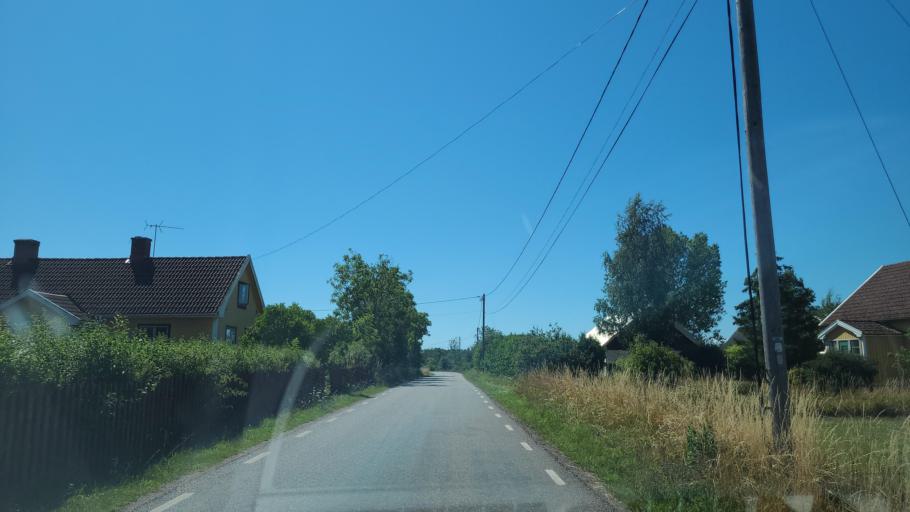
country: SE
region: Kalmar
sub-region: Borgholms Kommun
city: Borgholm
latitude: 56.7686
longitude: 16.6508
